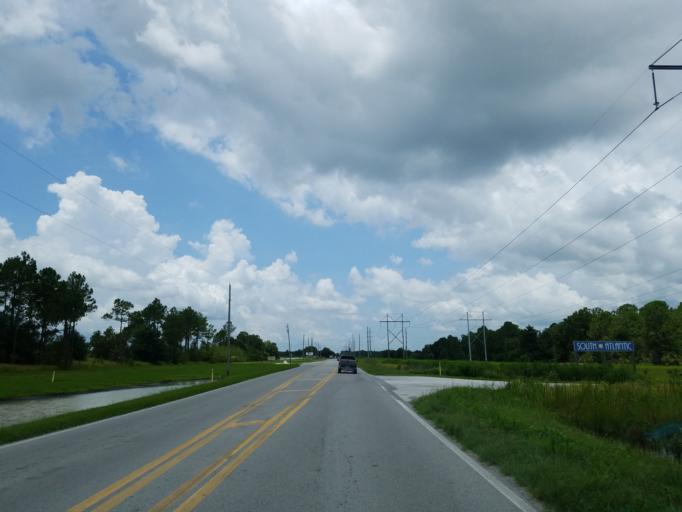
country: US
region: Florida
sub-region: Polk County
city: Willow Oak
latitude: 27.8507
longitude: -82.0506
